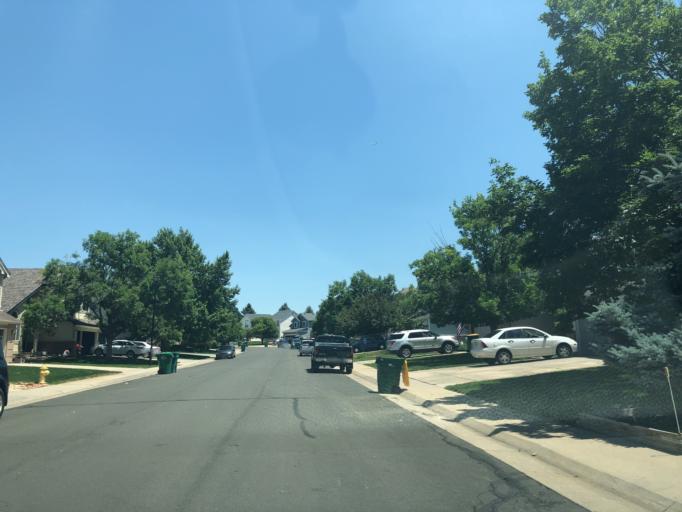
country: US
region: Colorado
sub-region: Arapahoe County
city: Dove Valley
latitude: 39.6277
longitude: -104.7685
